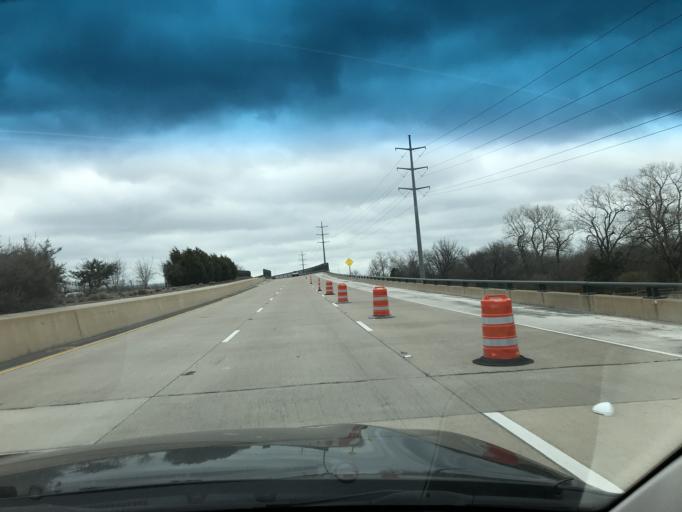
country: US
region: Texas
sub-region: Tarrant County
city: Westworth
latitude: 32.7156
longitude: -97.3908
